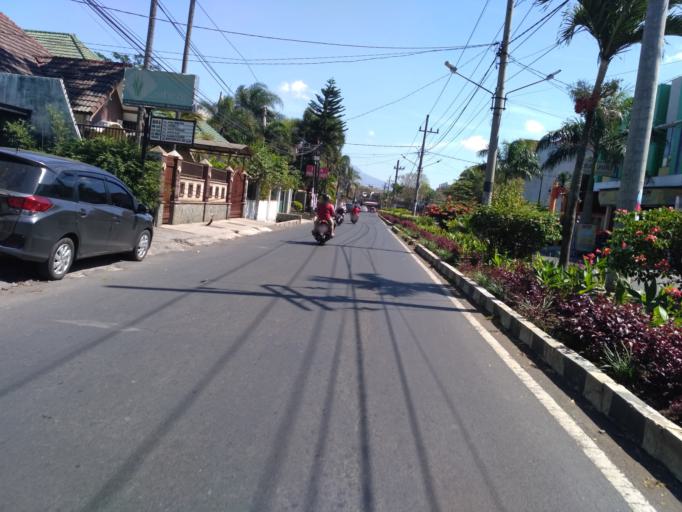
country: ID
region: East Java
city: Malang
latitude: -7.9802
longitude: 112.6615
